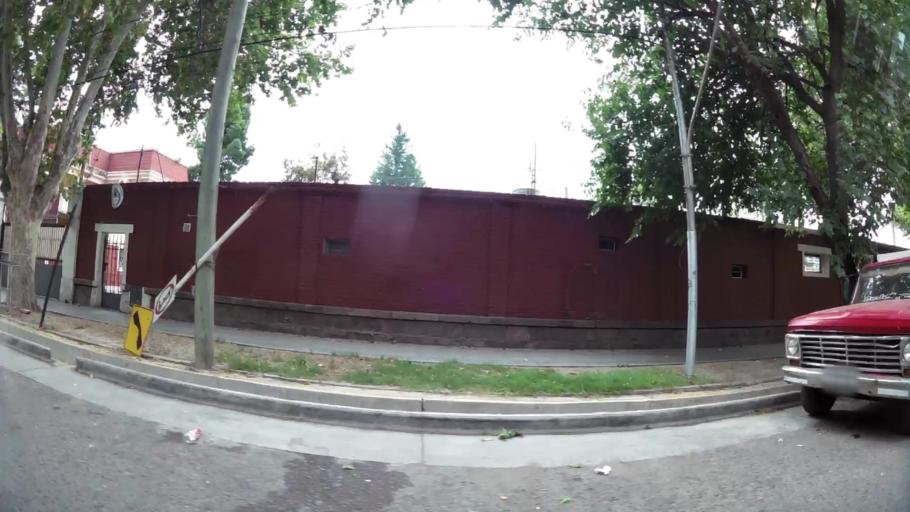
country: AR
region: Mendoza
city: Mendoza
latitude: -32.8970
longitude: -68.8514
